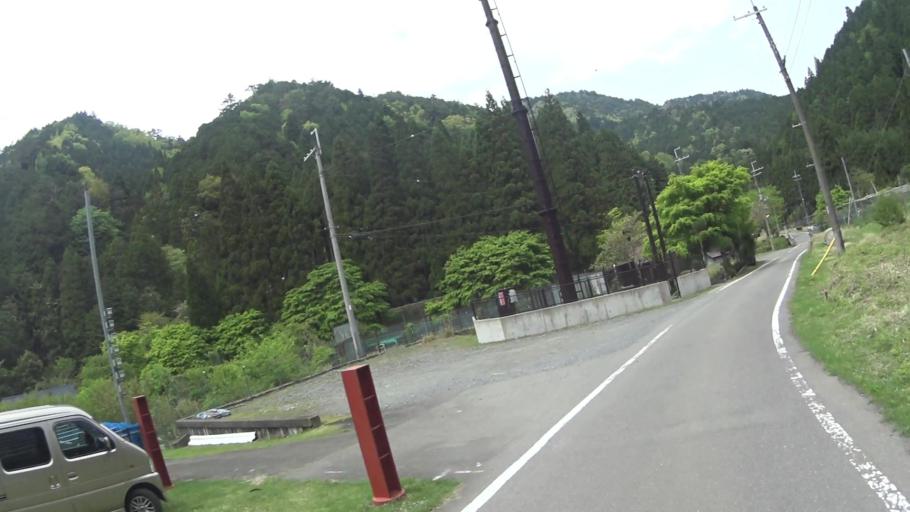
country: JP
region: Kyoto
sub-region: Kyoto-shi
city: Kamigyo-ku
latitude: 35.1873
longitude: 135.7340
